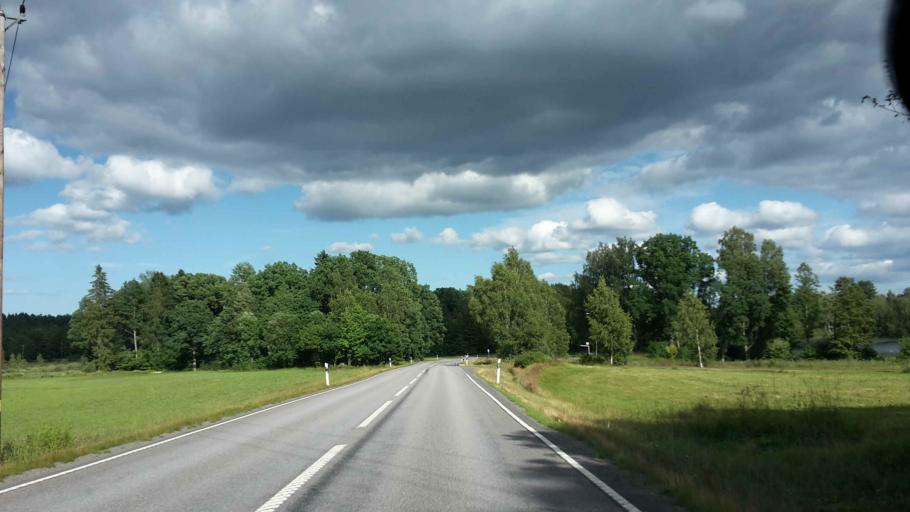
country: SE
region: OErebro
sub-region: Hallsbergs Kommun
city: Palsboda
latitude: 58.8018
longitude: 15.4468
